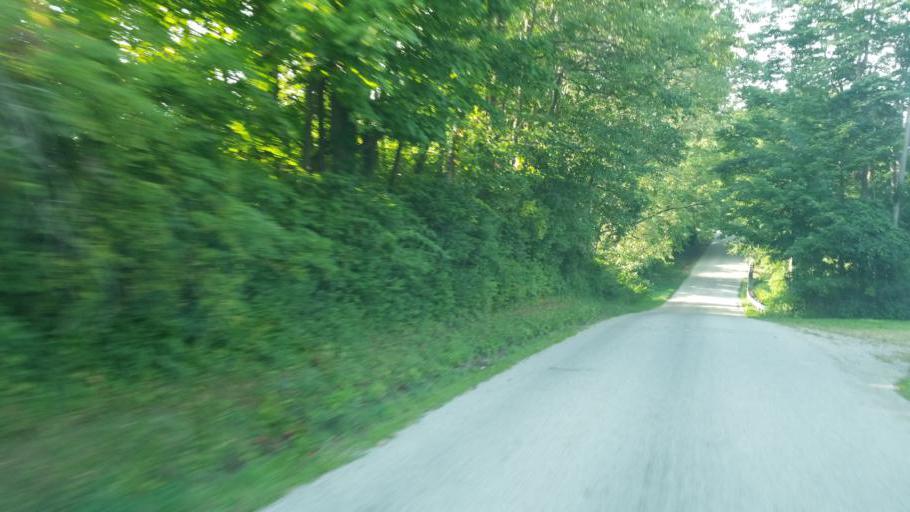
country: US
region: Ohio
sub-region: Sandusky County
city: Bellville
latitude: 40.6171
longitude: -82.4811
